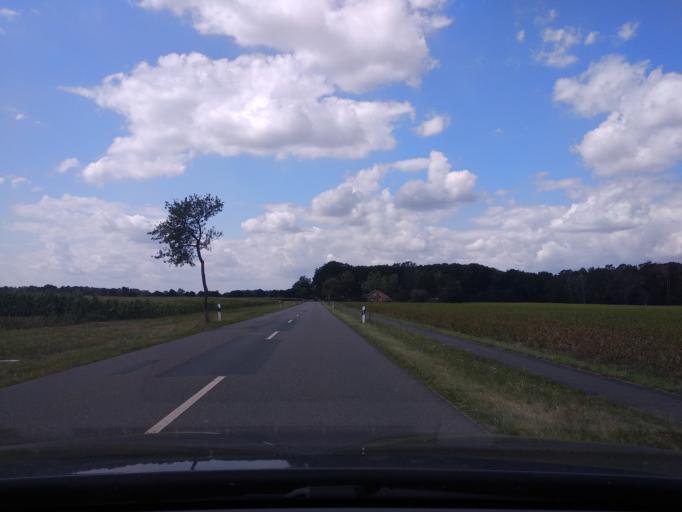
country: DE
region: Lower Saxony
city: Wagenhoff
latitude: 52.5087
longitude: 10.5120
